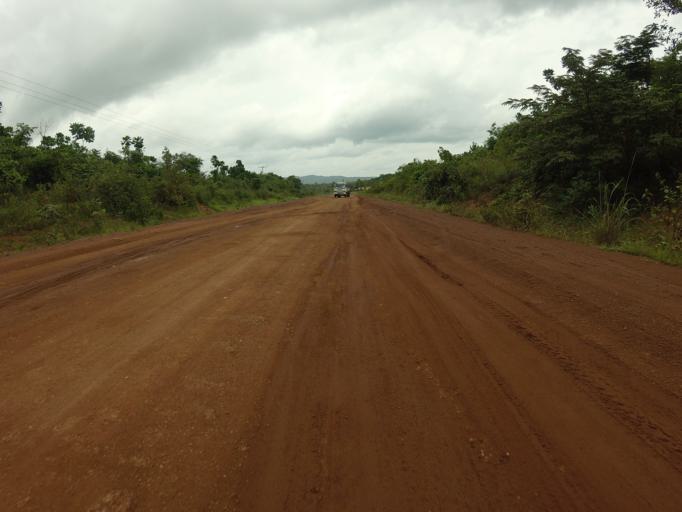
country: GH
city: Kpandae
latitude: 8.3016
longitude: 0.4860
